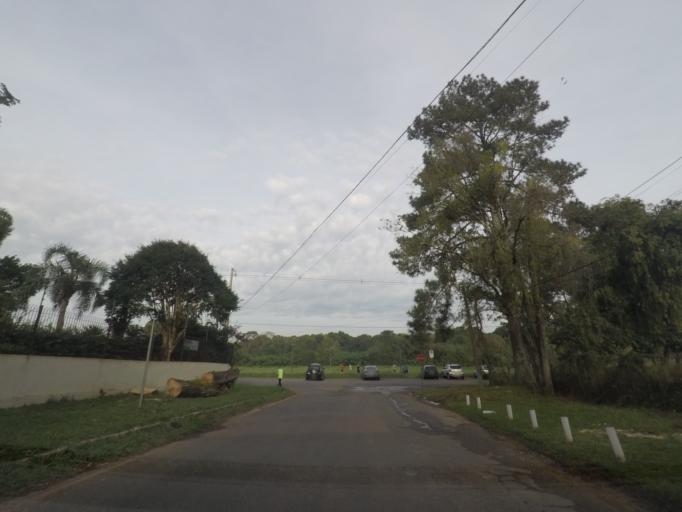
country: BR
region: Parana
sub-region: Curitiba
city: Curitiba
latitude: -25.4268
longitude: -49.3048
